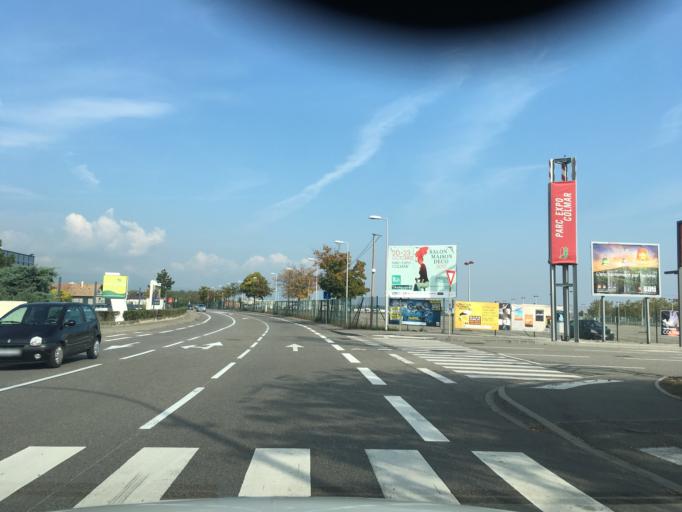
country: FR
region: Alsace
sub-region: Departement du Haut-Rhin
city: Colmar
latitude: 48.0965
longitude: 7.3566
